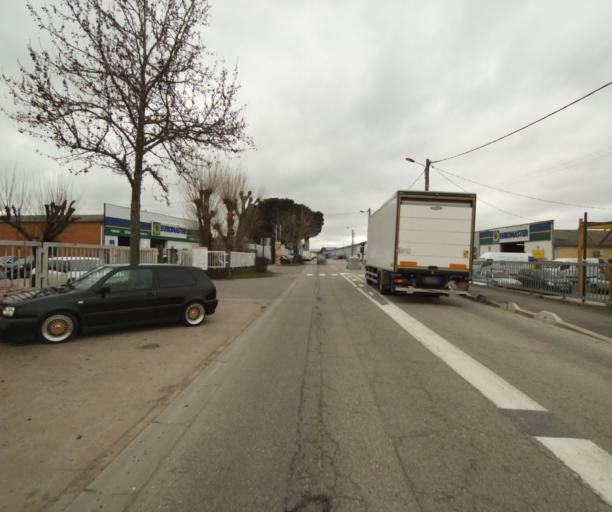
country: FR
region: Midi-Pyrenees
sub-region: Departement de l'Ariege
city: Pamiers
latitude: 43.1226
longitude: 1.6210
